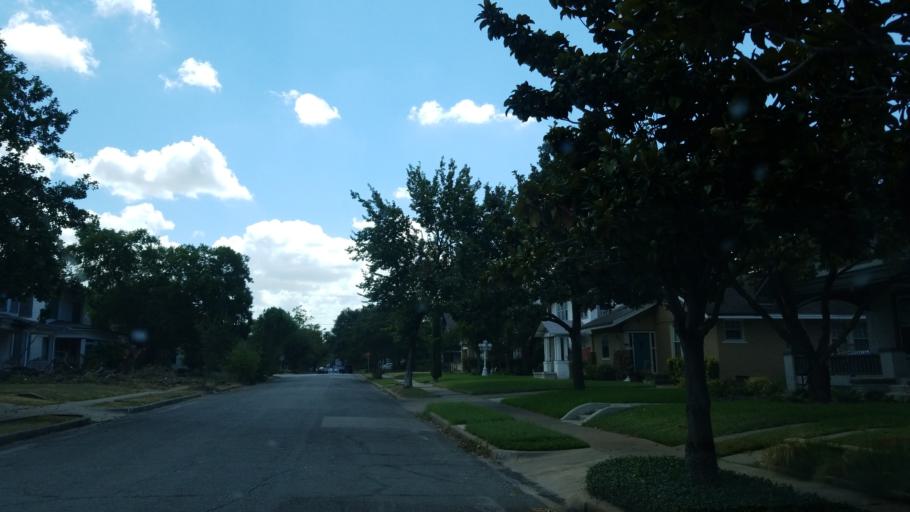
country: US
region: Texas
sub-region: Dallas County
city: Dallas
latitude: 32.7531
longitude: -96.8303
